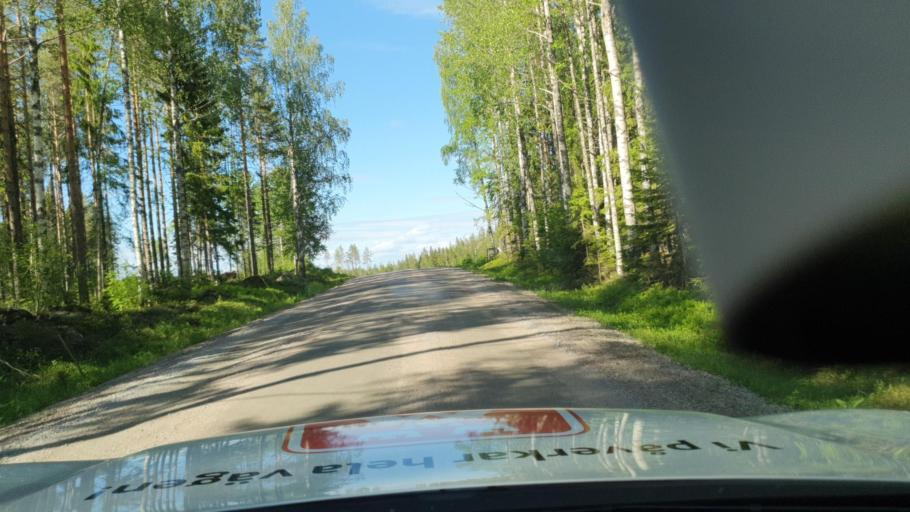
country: SE
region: Vaesterbotten
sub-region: Vannas Kommun
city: Vaennaes
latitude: 63.7894
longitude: 19.6243
